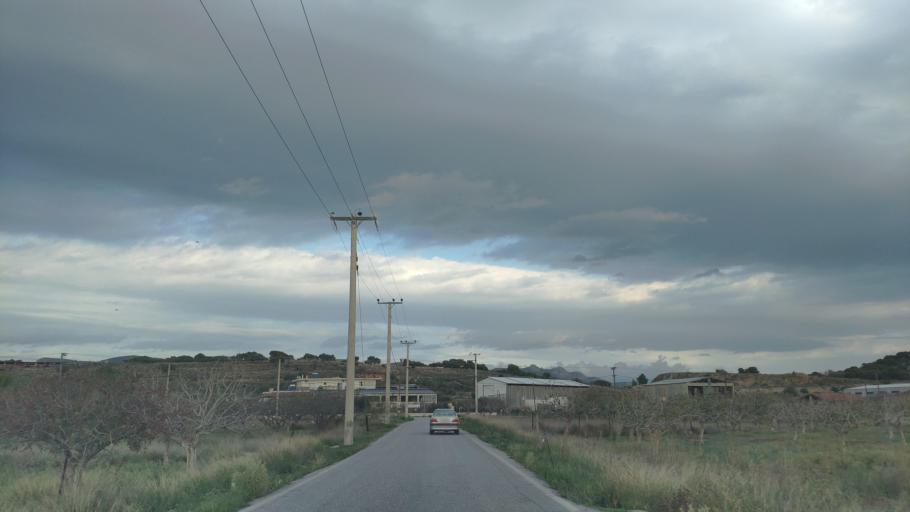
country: GR
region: Attica
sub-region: Nomarchia Dytikis Attikis
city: Nea Peramos
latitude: 37.9928
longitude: 23.3959
